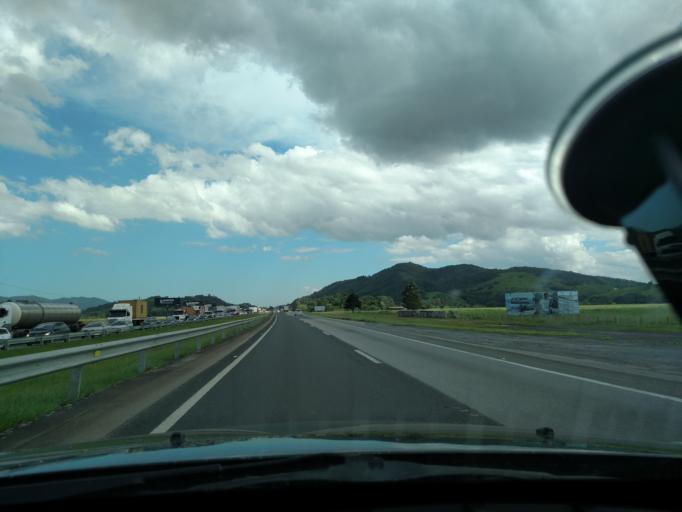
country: BR
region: Santa Catarina
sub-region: Tijucas
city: Tijucas
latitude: -27.2658
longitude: -48.6319
